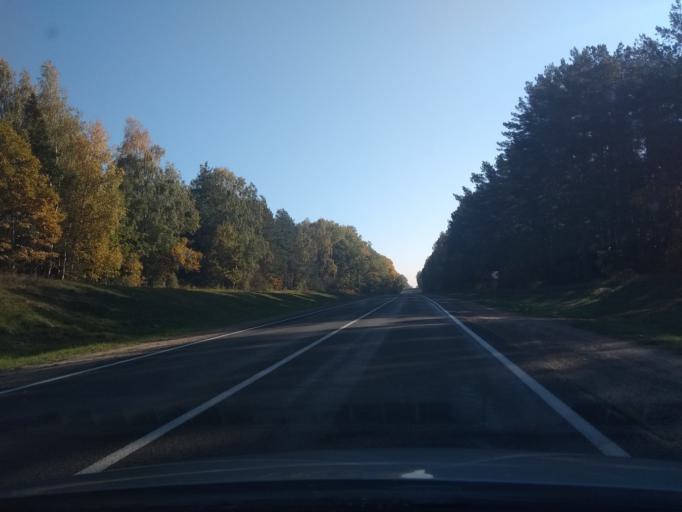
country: BY
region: Grodnenskaya
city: Zel'va
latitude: 53.1414
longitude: 24.8939
